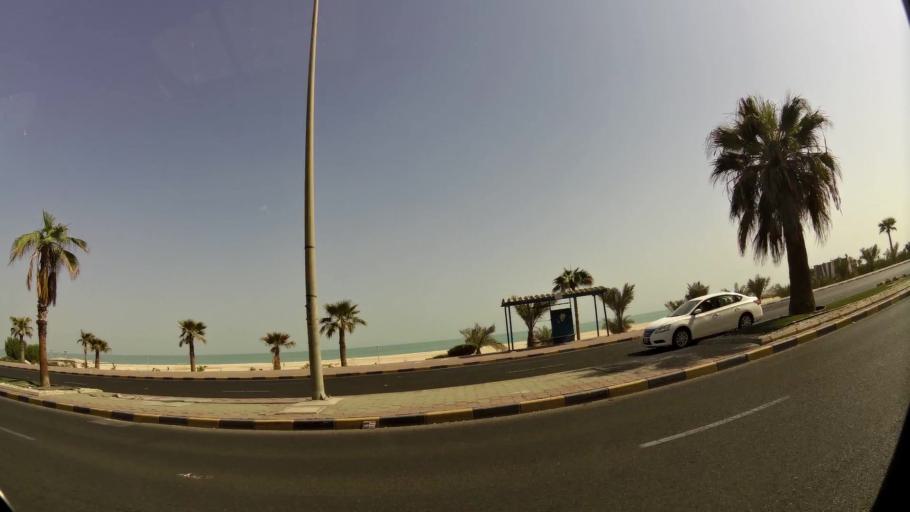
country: KW
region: Muhafazat Hawalli
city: As Salimiyah
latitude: 29.3303
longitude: 48.0916
